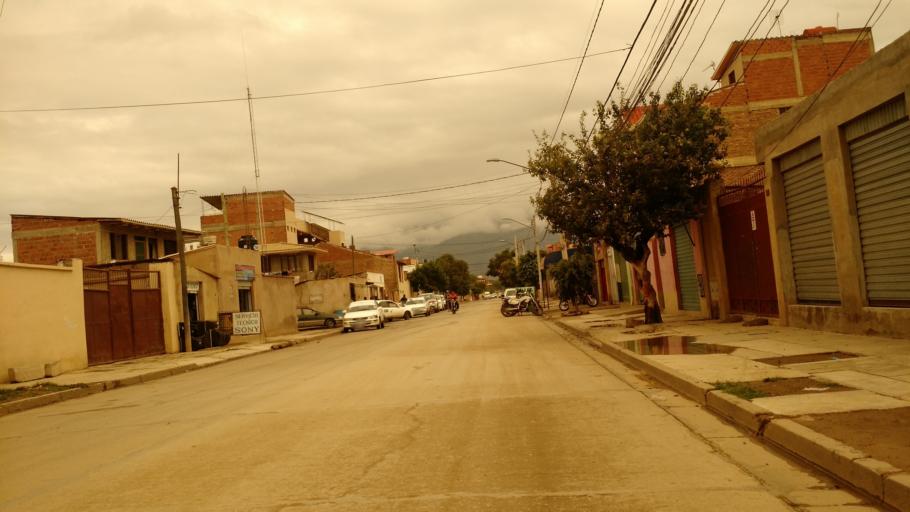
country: BO
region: Cochabamba
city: Cochabamba
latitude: -17.4355
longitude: -66.1551
